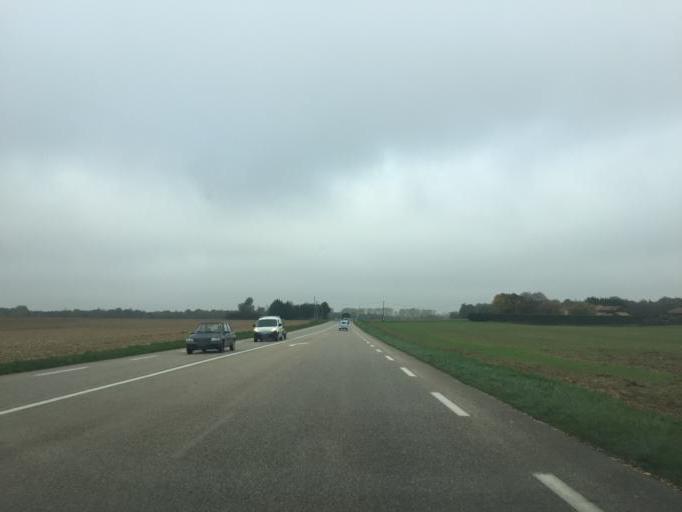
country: FR
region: Rhone-Alpes
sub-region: Departement de l'Ain
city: Villars-les-Dombes
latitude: 45.9620
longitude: 5.0034
